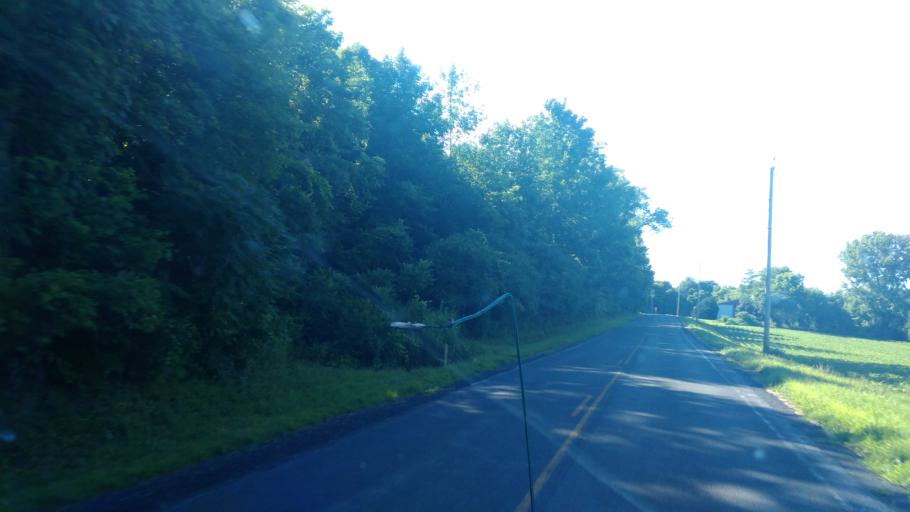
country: US
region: New York
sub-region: Wayne County
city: Lyons
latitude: 43.0087
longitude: -76.9751
